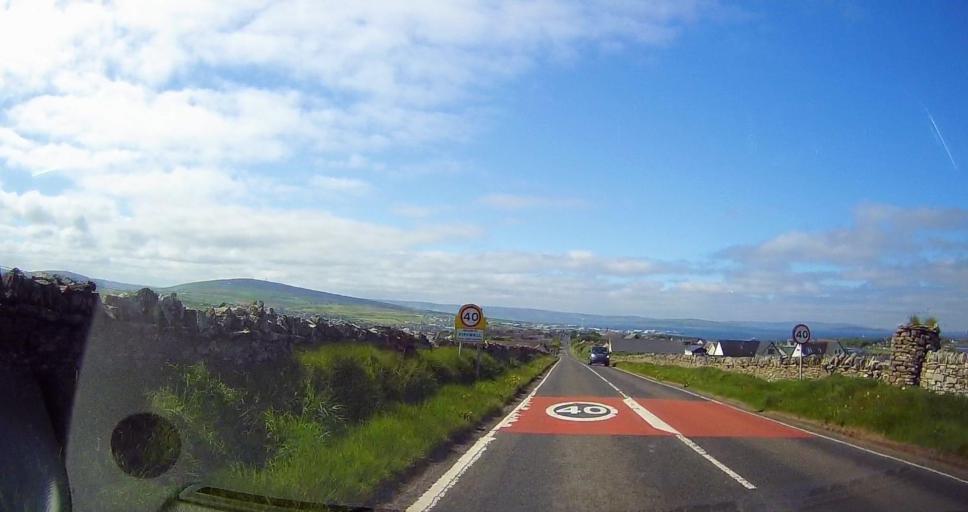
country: GB
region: Scotland
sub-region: Orkney Islands
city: Kirkwall
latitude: 58.9680
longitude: -2.9432
